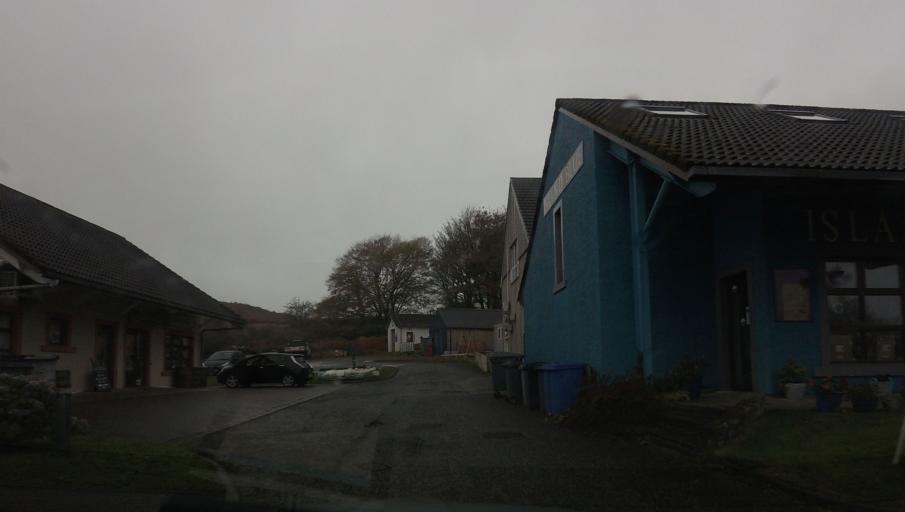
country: GB
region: Scotland
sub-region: Argyll and Bute
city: Isle Of Mull
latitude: 56.6148
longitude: -6.0710
